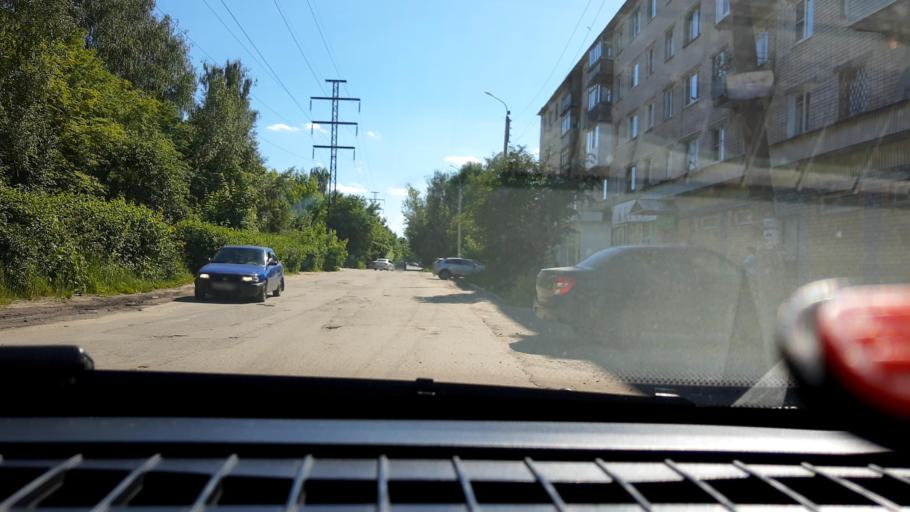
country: RU
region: Nizjnij Novgorod
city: Gidrotorf
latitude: 56.5205
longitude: 43.5557
